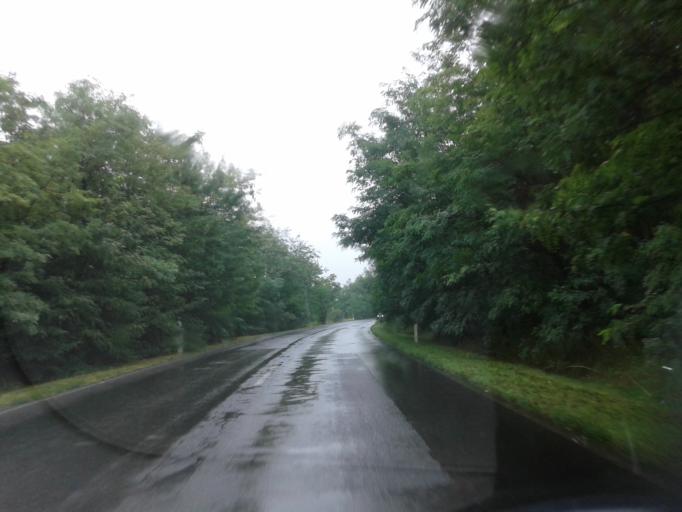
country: HU
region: Csongrad
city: Asotthalom
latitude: 46.2295
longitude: 19.7535
